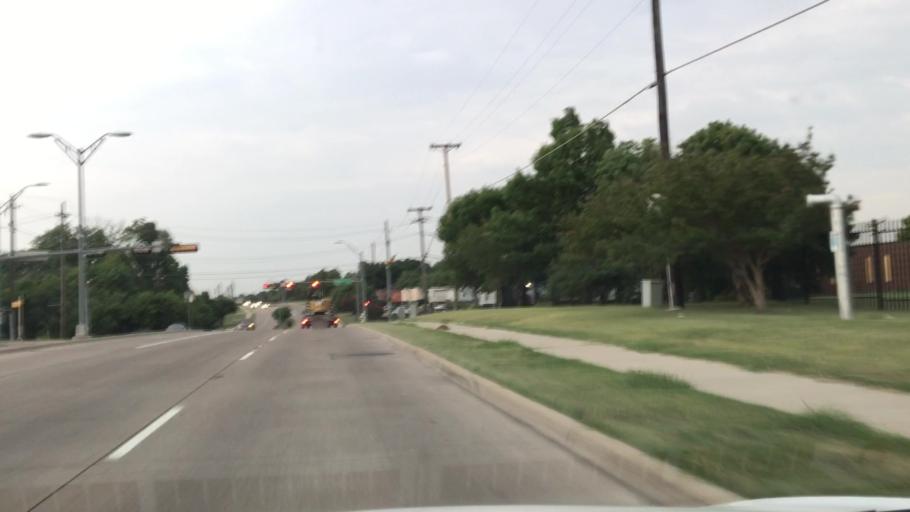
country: US
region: Texas
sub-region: Dallas County
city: Highland Park
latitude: 32.7929
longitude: -96.7133
